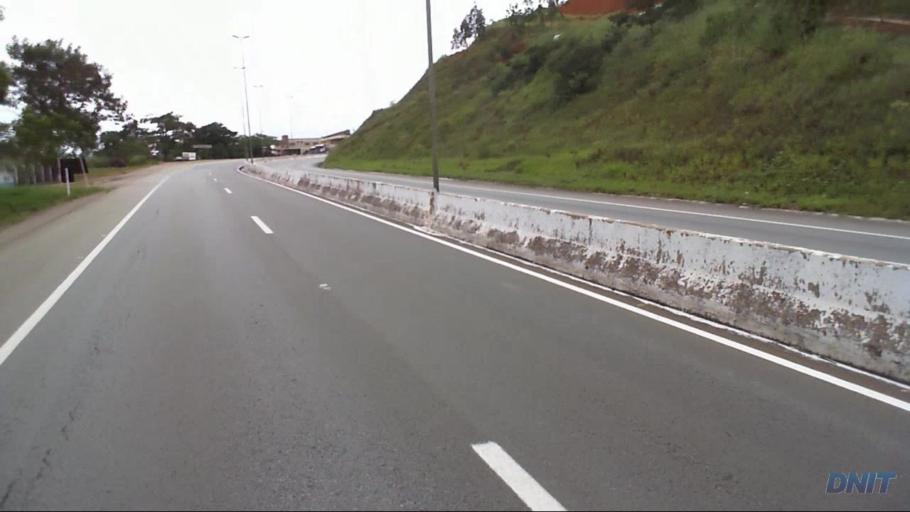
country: BR
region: Minas Gerais
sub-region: Nova Era
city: Nova Era
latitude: -19.7619
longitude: -43.0373
